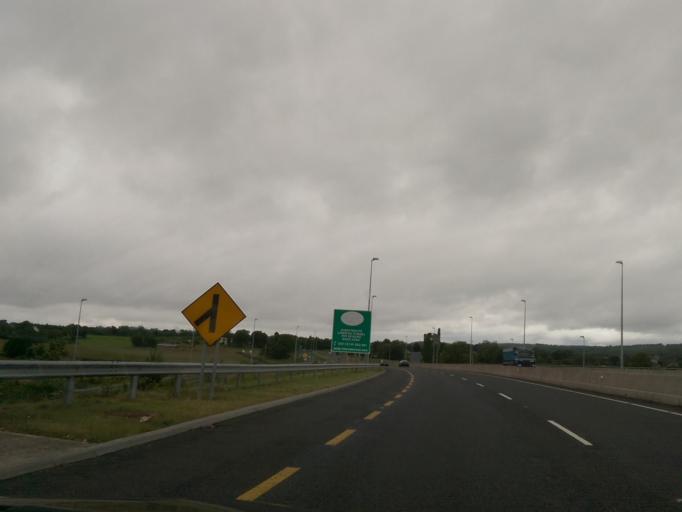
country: IE
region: Munster
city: Moyross
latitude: 52.6826
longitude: -8.7155
